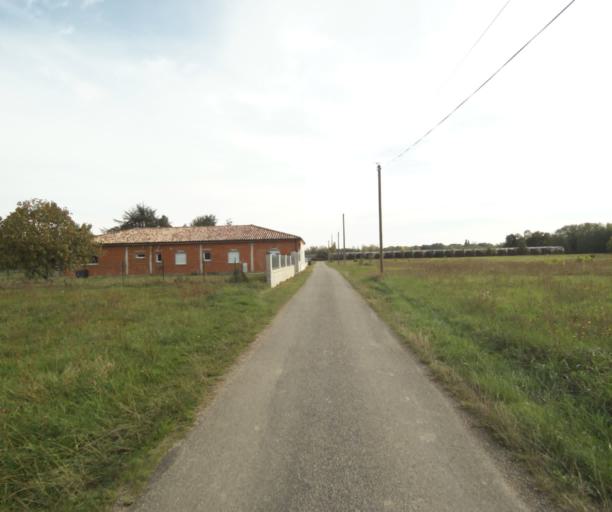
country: FR
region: Midi-Pyrenees
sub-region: Departement du Tarn-et-Garonne
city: Labastide-Saint-Pierre
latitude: 43.9291
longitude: 1.3561
